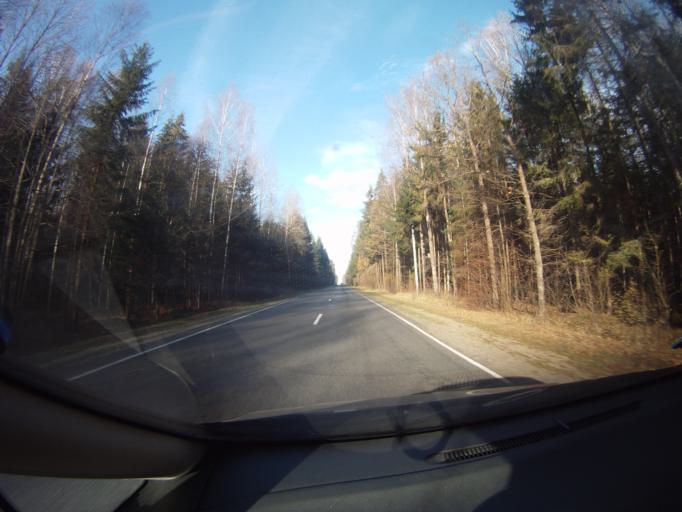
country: BY
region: Minsk
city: Il'ya
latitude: 54.3718
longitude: 27.3922
